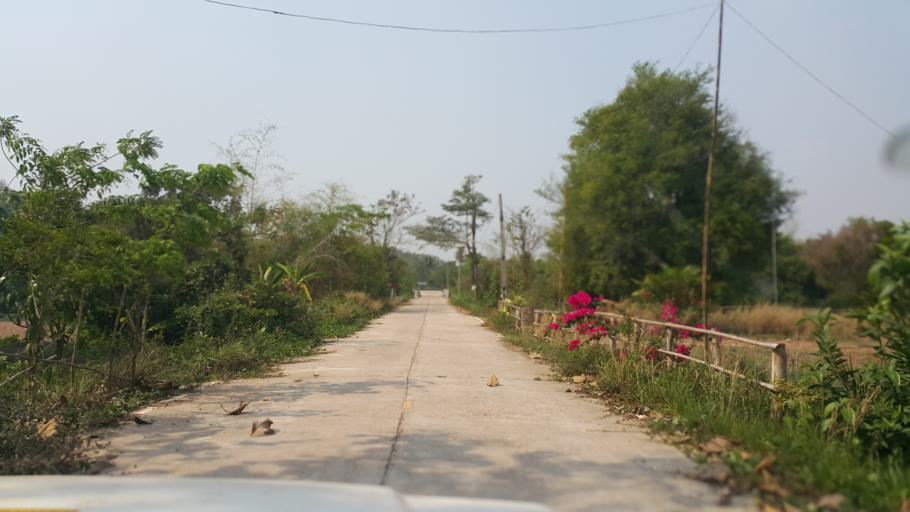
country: TH
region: Nakhon Phanom
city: Ban Phaeng
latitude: 17.9846
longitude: 104.1455
